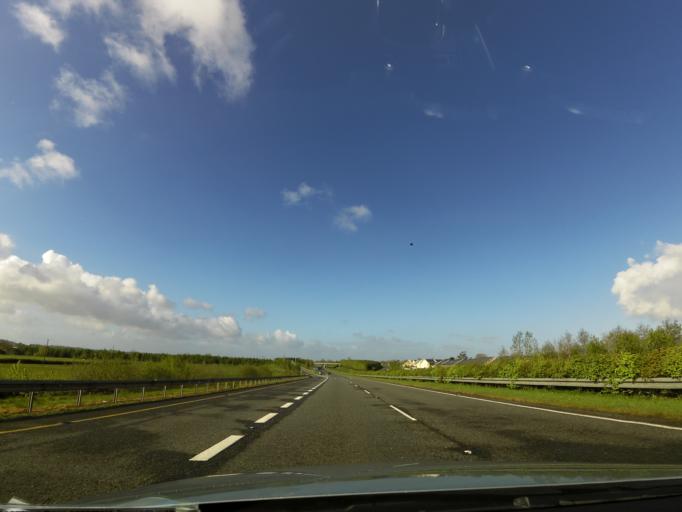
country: IE
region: Munster
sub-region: County Limerick
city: Annacotty
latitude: 52.6510
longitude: -8.5576
